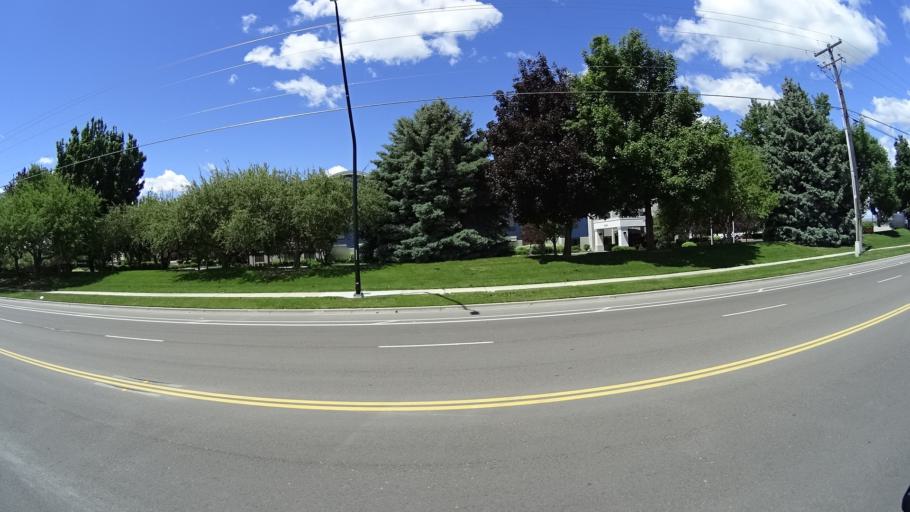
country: US
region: Idaho
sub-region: Ada County
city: Eagle
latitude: 43.6624
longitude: -116.3346
